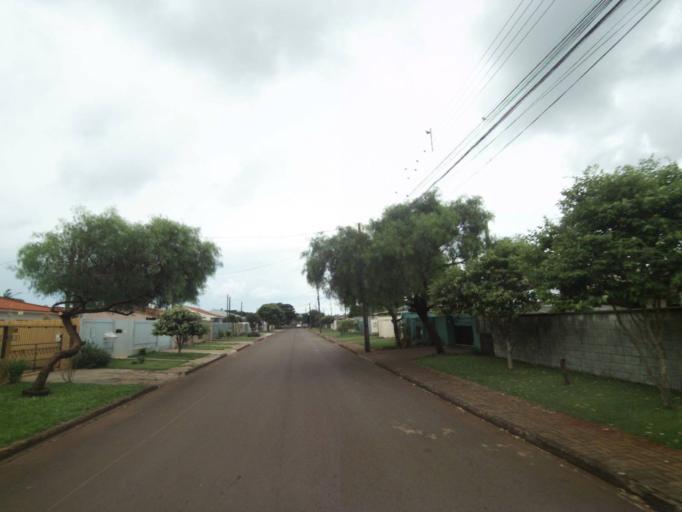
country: BR
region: Parana
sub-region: Campo Mourao
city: Campo Mourao
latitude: -24.0224
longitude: -52.3580
